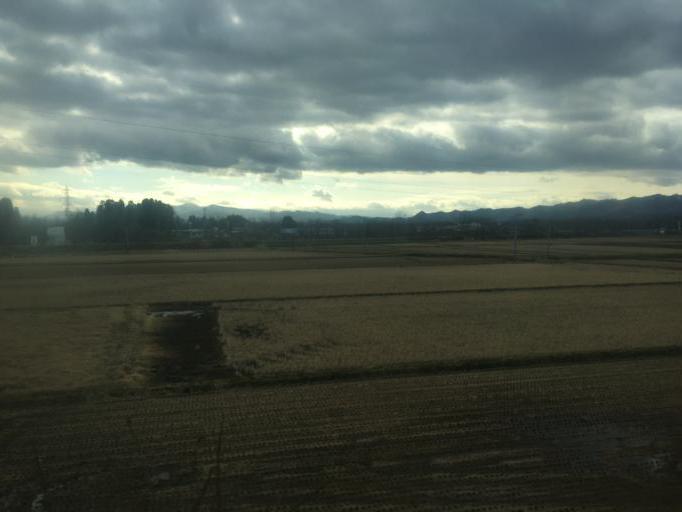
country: JP
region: Akita
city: Odate
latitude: 40.2806
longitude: 140.5172
